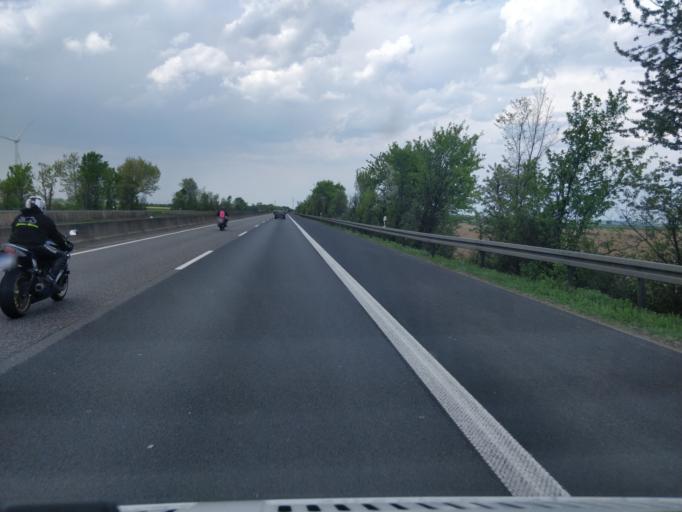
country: DE
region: North Rhine-Westphalia
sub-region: Regierungsbezirk Koln
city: Euskirchen
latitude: 50.7091
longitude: 6.7747
